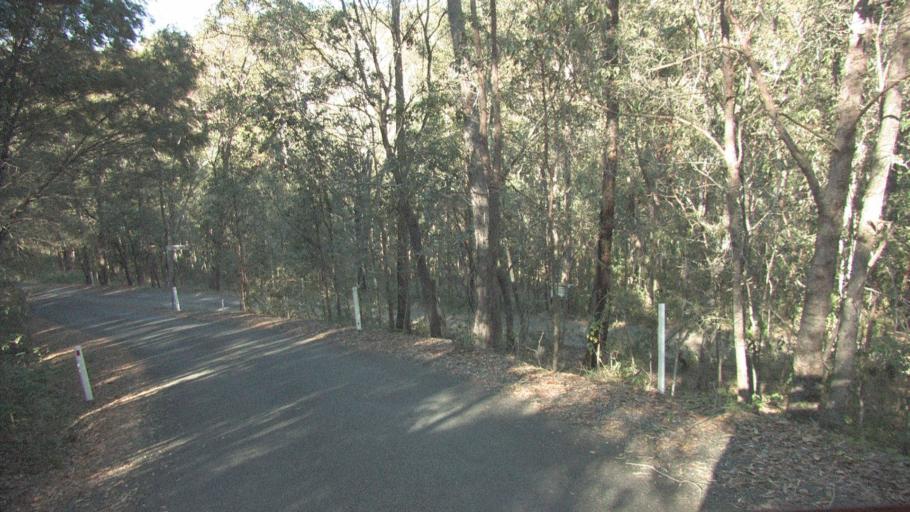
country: AU
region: Queensland
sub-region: Logan
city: Windaroo
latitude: -27.7928
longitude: 153.1702
